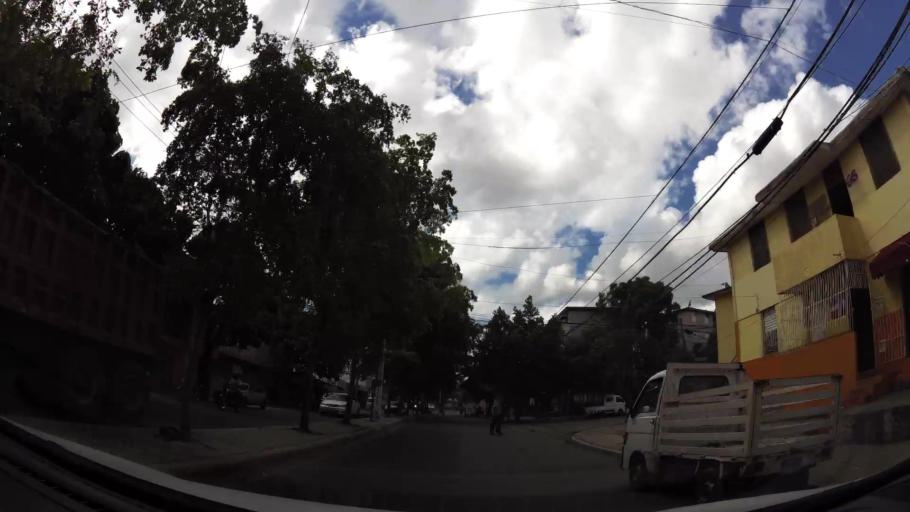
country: DO
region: Nacional
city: San Carlos
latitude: 18.4912
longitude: -69.8837
